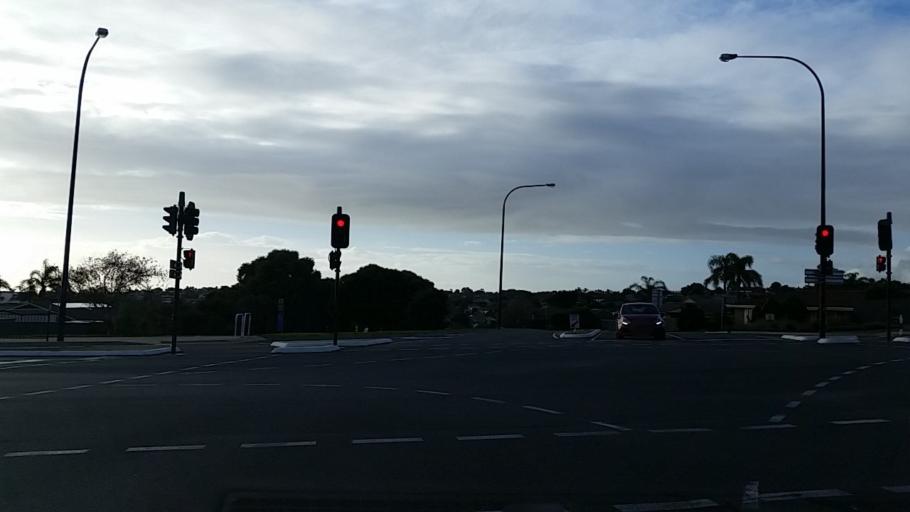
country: AU
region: South Australia
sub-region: Marion
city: Happy Valley
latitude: -35.0775
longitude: 138.5146
